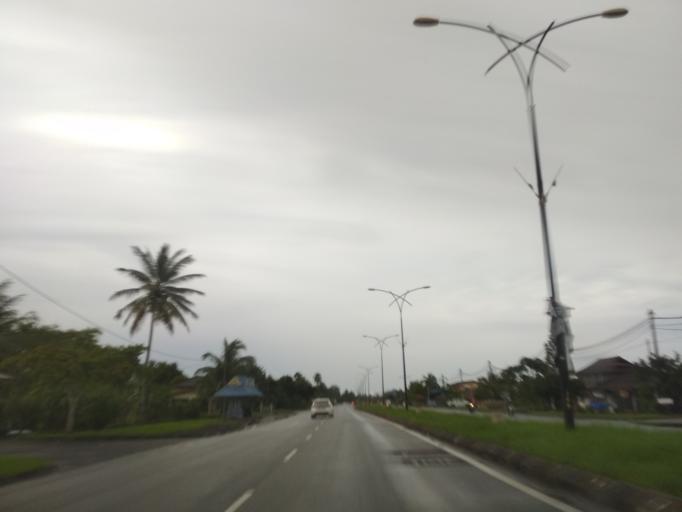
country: MY
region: Perlis
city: Kangar
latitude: 6.4595
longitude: 100.2081
